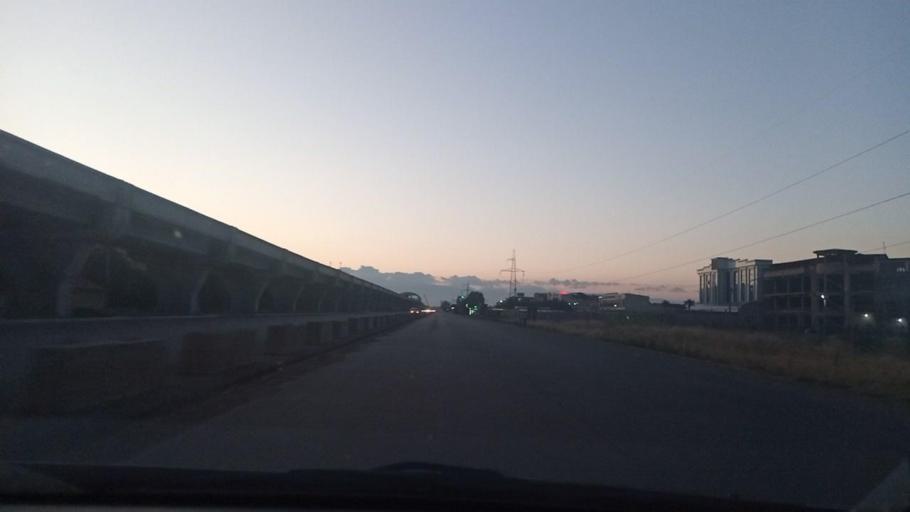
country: UZ
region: Toshkent Shahri
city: Bektemir
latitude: 41.2441
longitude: 69.2914
